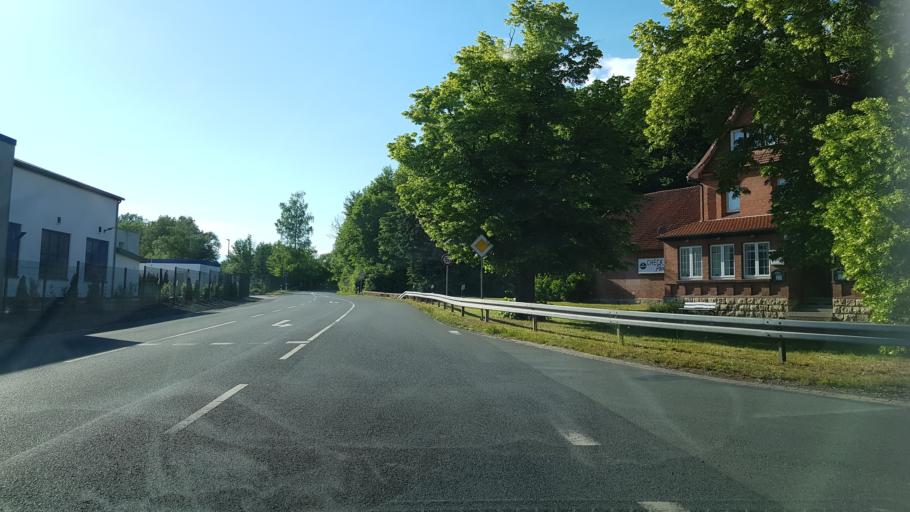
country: DE
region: Lower Saxony
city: Coppengrave
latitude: 51.9800
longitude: 9.7462
